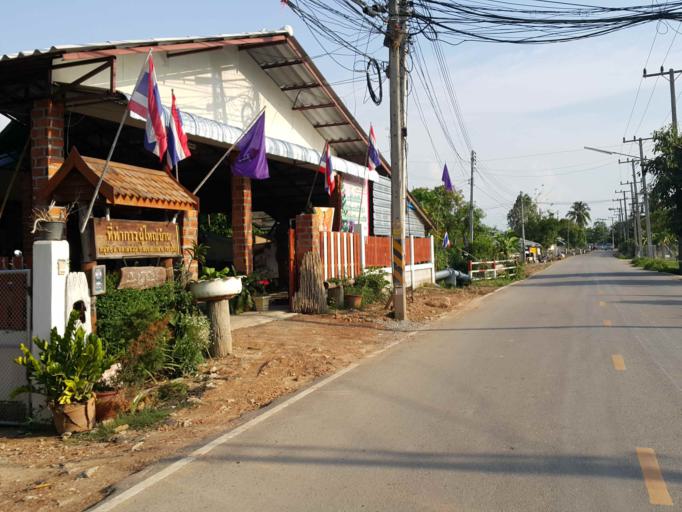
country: TH
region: Chiang Mai
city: San Sai
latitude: 18.8415
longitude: 99.0817
